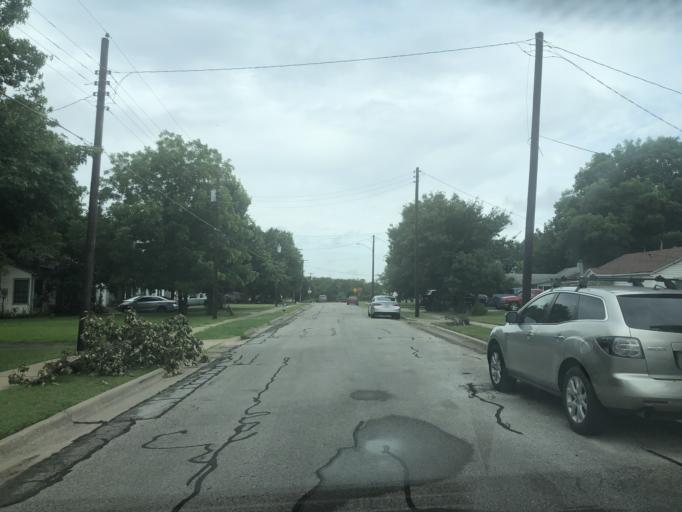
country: US
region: Texas
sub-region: Dallas County
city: Irving
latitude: 32.8074
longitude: -96.9478
